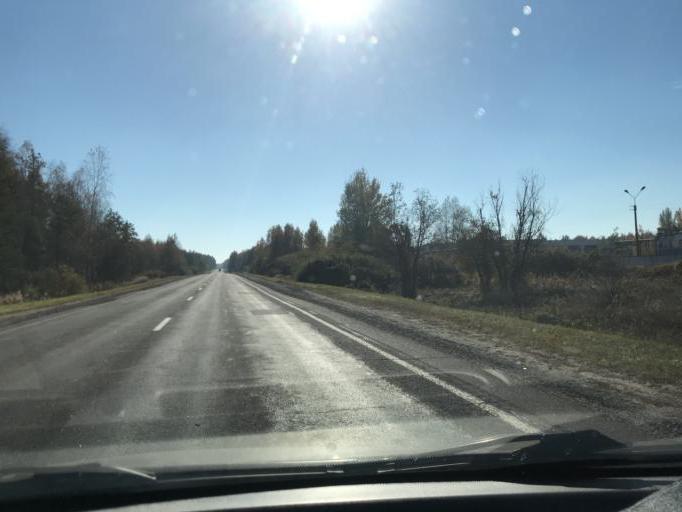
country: BY
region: Gomel
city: Kastsyukowka
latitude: 52.4418
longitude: 30.8254
